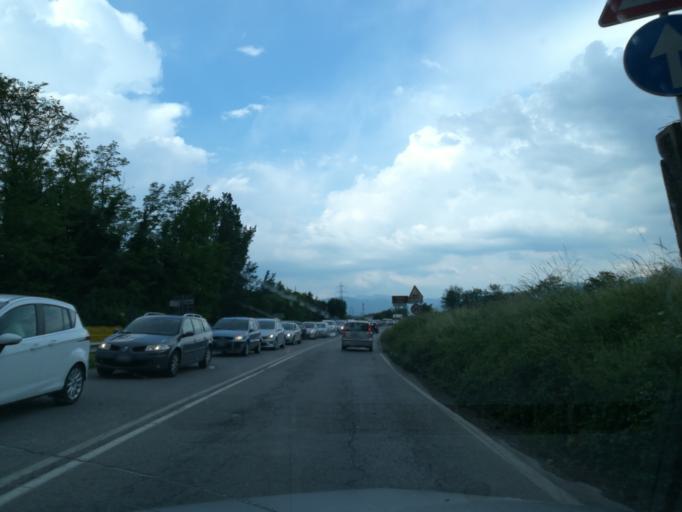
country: IT
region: Lombardy
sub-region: Provincia di Bergamo
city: Mozzo
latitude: 45.6950
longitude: 9.6028
